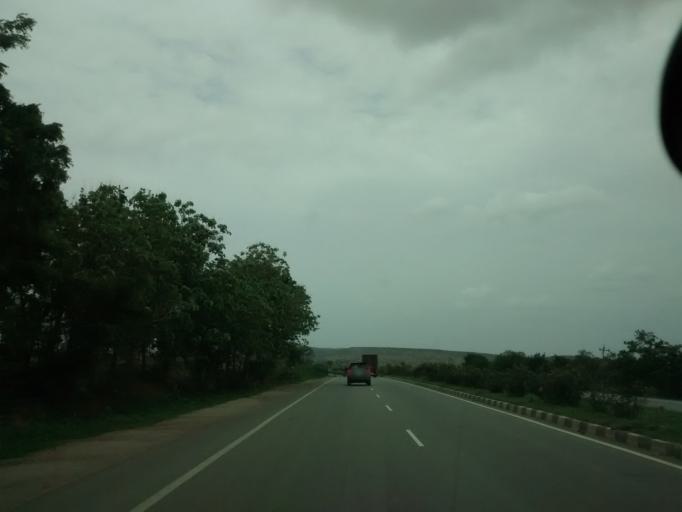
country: IN
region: Andhra Pradesh
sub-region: Kurnool
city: Ramapuram
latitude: 15.2571
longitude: 77.7578
